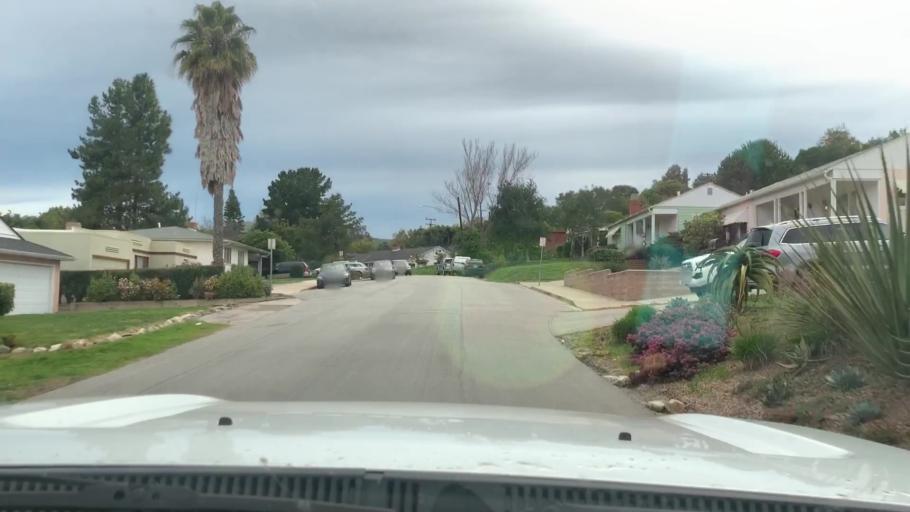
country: US
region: California
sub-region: San Luis Obispo County
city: San Luis Obispo
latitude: 35.2945
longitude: -120.6592
